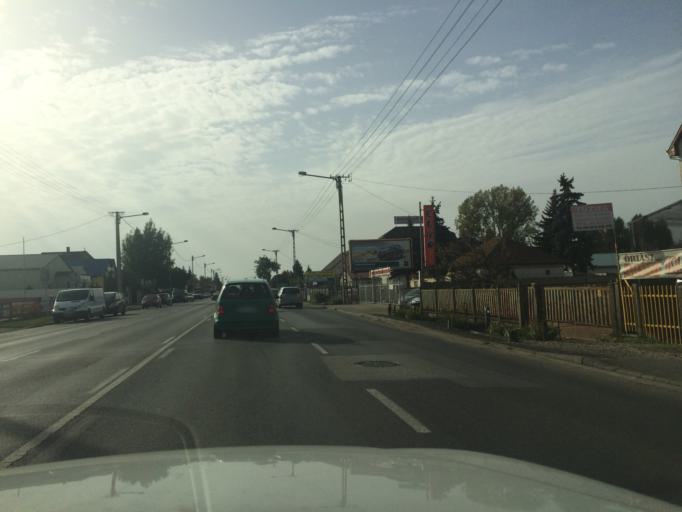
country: HU
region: Szabolcs-Szatmar-Bereg
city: Nyiregyhaza
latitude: 47.9284
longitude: 21.7188
